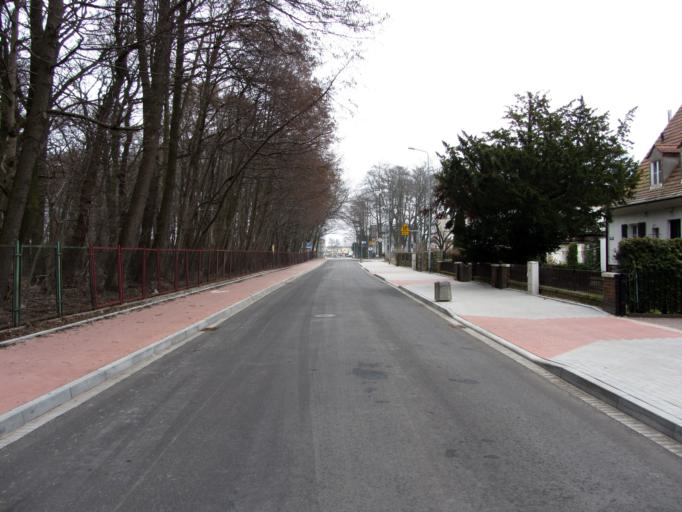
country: PL
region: West Pomeranian Voivodeship
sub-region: Powiat kolobrzeski
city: Kolobrzeg
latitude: 54.1782
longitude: 15.5463
